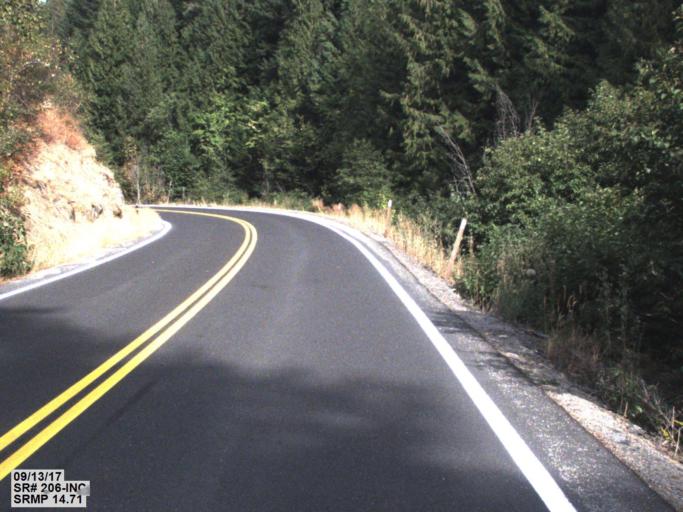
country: US
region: Washington
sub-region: Spokane County
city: Otis Orchards-East Farms
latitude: 47.8791
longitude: -117.1406
